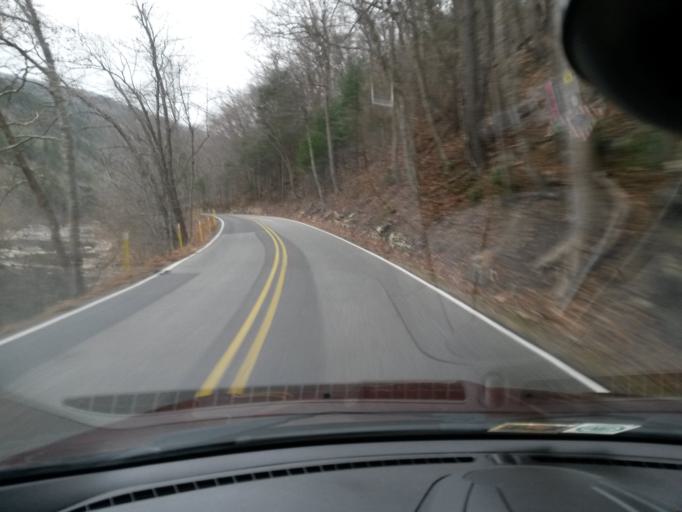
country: US
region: Virginia
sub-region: Rockbridge County
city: East Lexington
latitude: 37.9464
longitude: -79.4601
